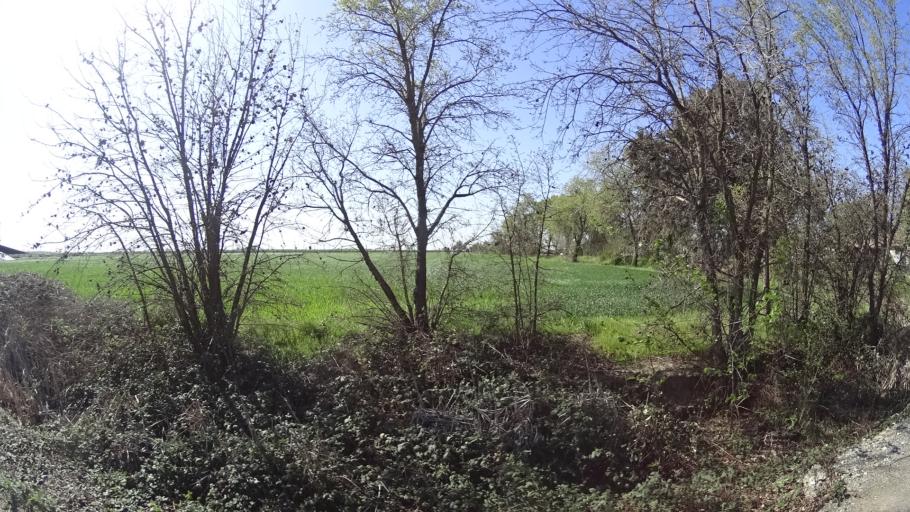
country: US
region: California
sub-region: Glenn County
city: Hamilton City
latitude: 39.7824
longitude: -122.0546
